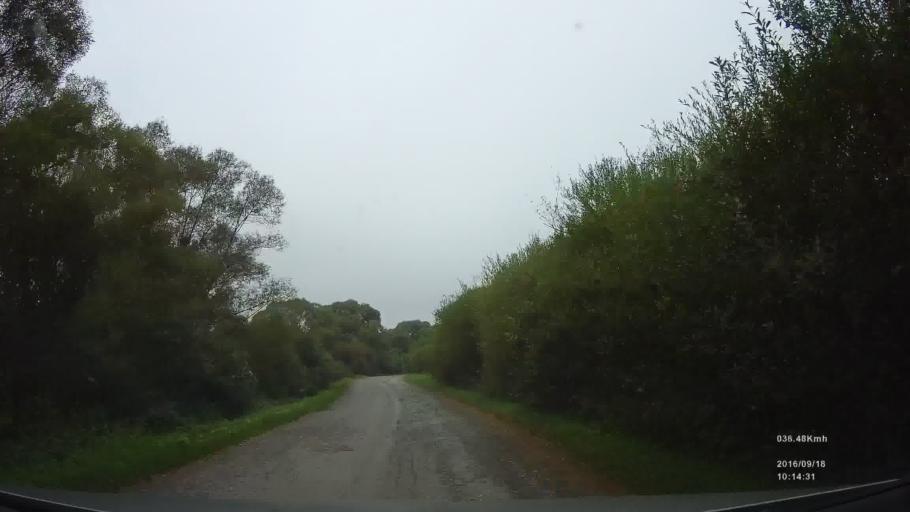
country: SK
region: Kosicky
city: Spisska Nova Ves
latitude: 48.9409
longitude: 20.6259
